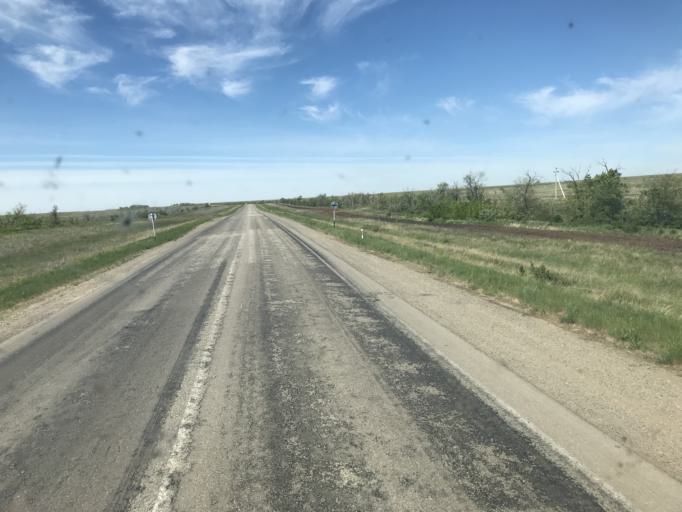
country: KZ
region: Aqtoebe
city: Martuk
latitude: 50.2283
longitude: 56.6343
